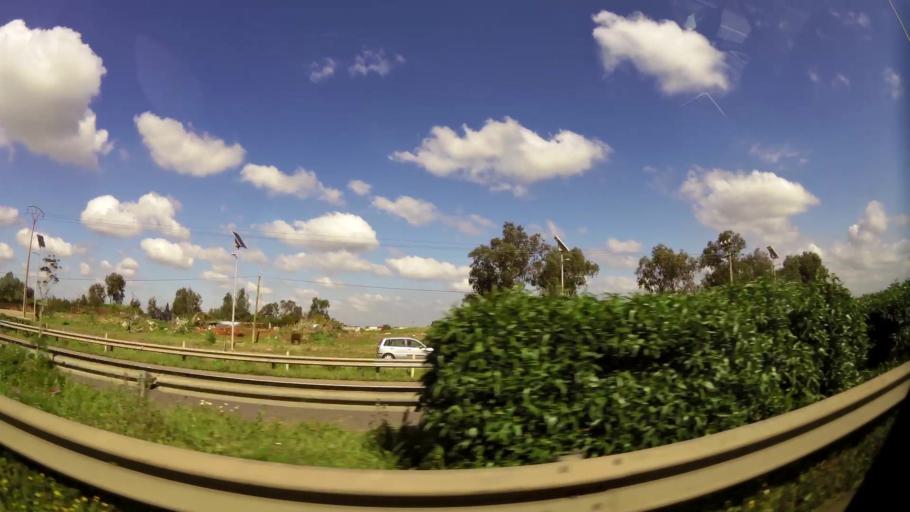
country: MA
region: Chaouia-Ouardigha
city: Nouaseur
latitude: 33.4166
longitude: -7.6267
